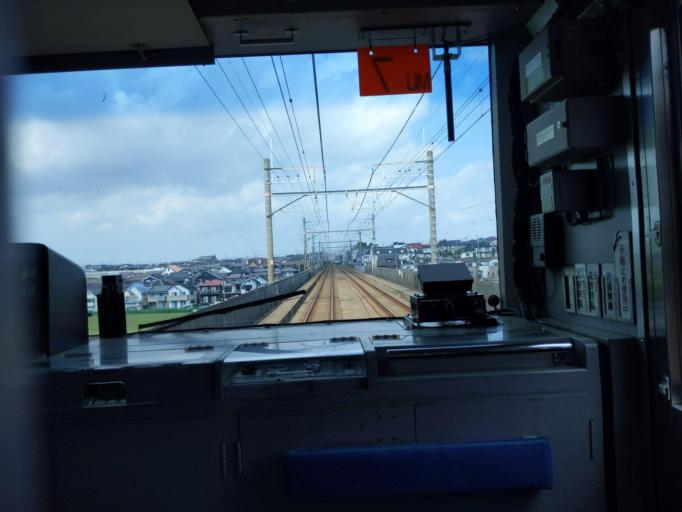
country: JP
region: Chiba
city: Matsudo
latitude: 35.8049
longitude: 139.9343
